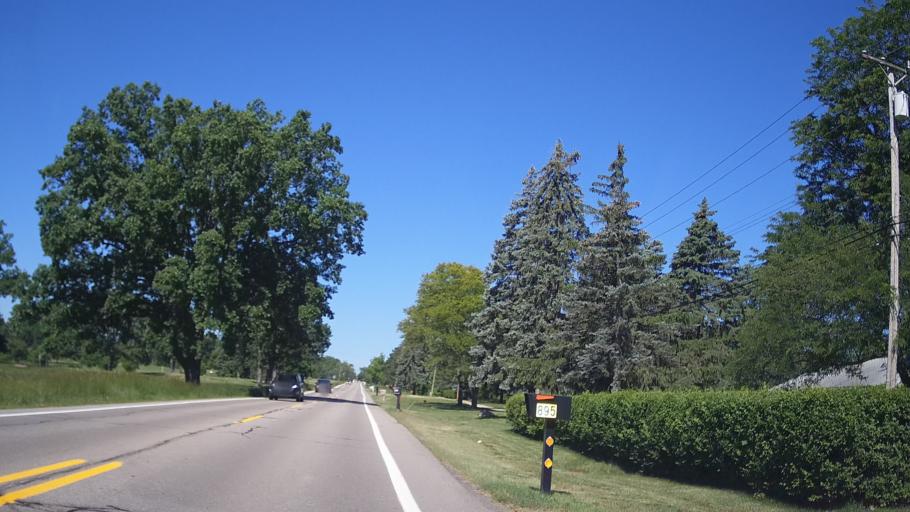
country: US
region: Michigan
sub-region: Oakland County
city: Troy
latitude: 42.6069
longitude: -83.1323
